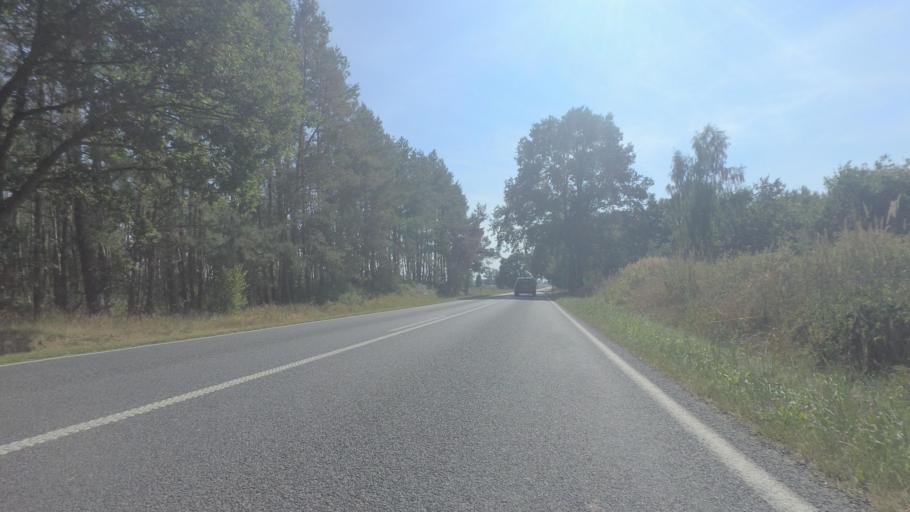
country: DE
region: Mecklenburg-Vorpommern
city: Brandshagen
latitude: 54.1632
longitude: 13.1705
